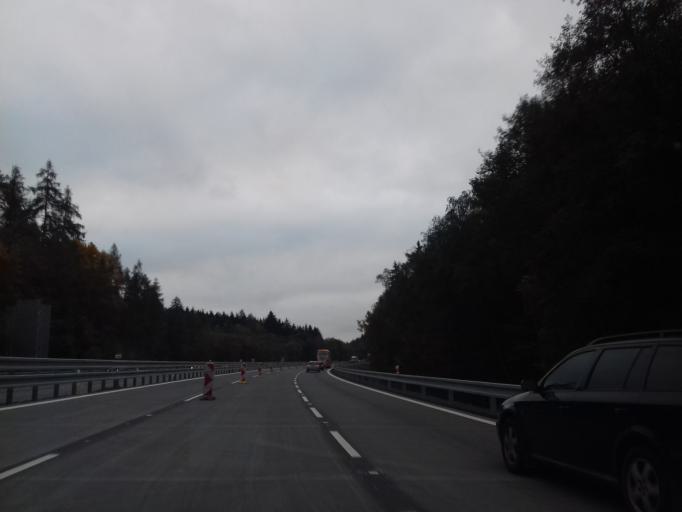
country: CZ
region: Central Bohemia
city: Ondrejov
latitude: 49.8546
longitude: 14.7967
